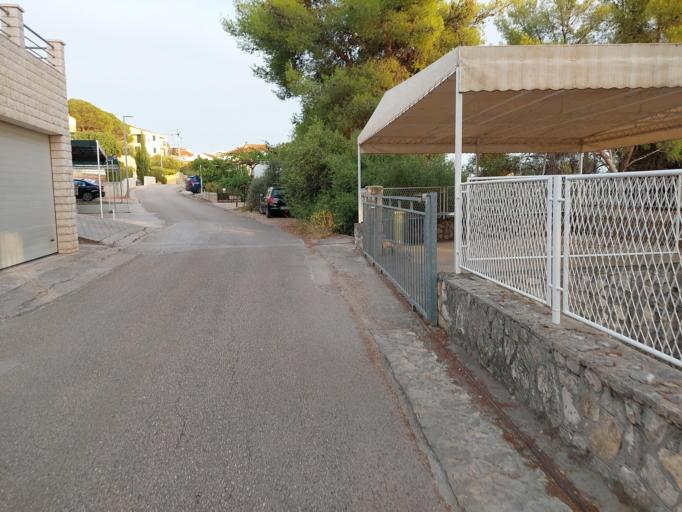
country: HR
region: Splitsko-Dalmatinska
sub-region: Grad Trogir
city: Trogir
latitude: 43.4927
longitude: 16.2753
